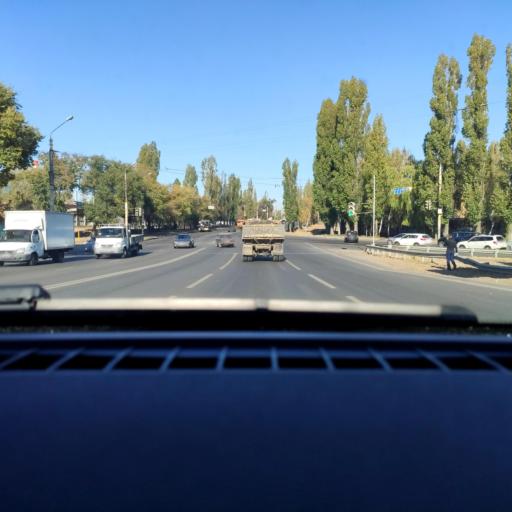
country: RU
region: Voronezj
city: Voronezh
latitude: 51.6235
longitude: 39.2339
